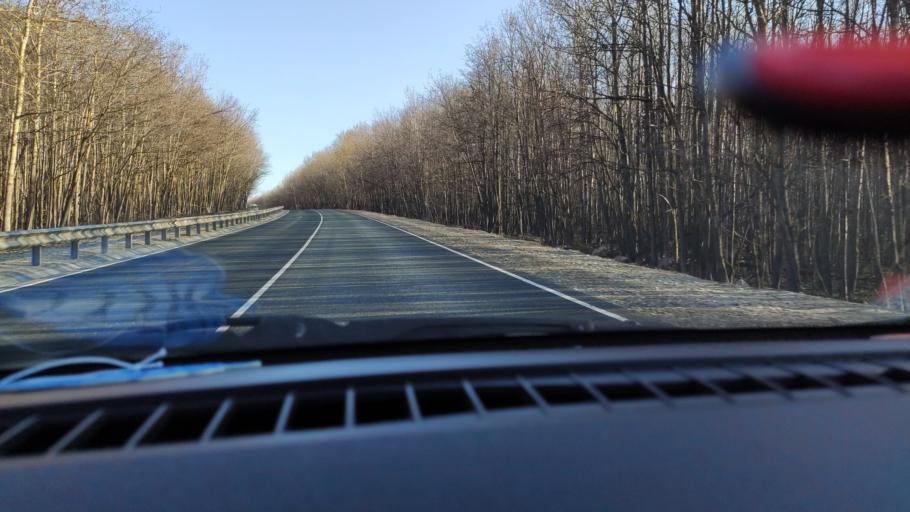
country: RU
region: Saratov
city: Khvalynsk
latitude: 52.4642
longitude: 48.0177
